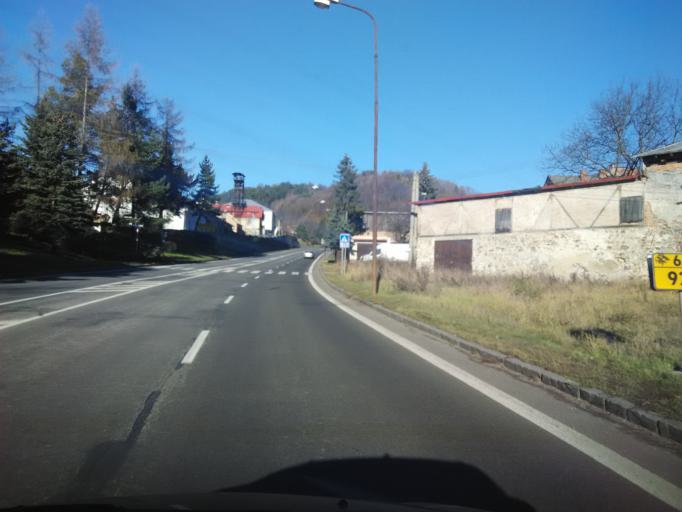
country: SK
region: Banskobystricky
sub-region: Okres Ziar nad Hronom
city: Kremnica
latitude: 48.7060
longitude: 18.9148
